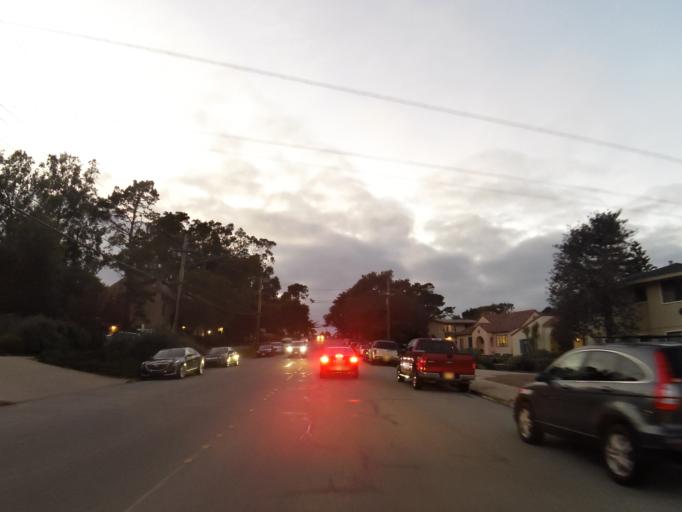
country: US
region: California
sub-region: Monterey County
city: Pacific Grove
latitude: 36.6252
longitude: -121.9263
